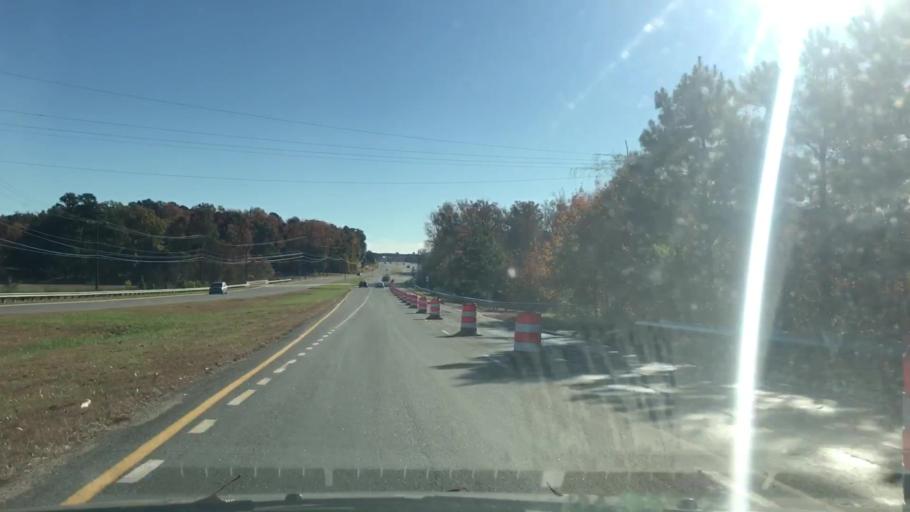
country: US
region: Virginia
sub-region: Henrico County
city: Short Pump
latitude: 37.6668
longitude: -77.6672
